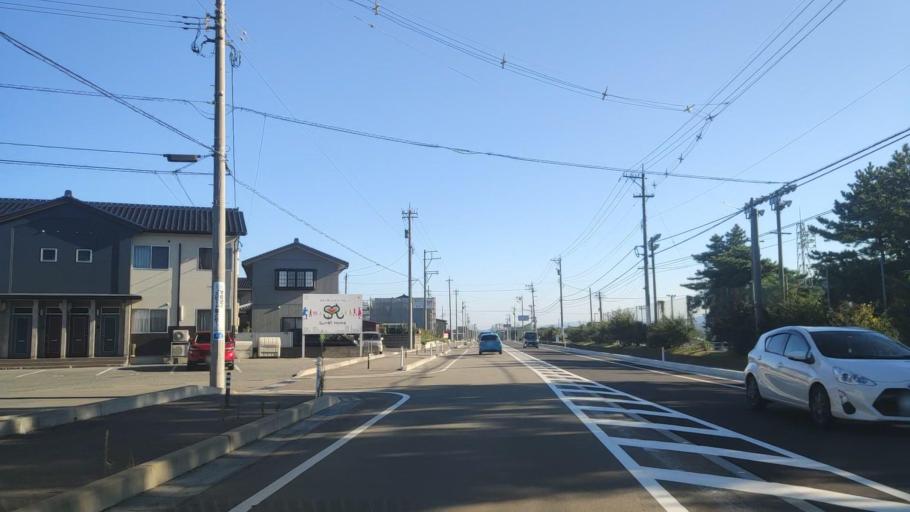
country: JP
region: Ishikawa
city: Tsubata
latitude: 36.7338
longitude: 136.7009
